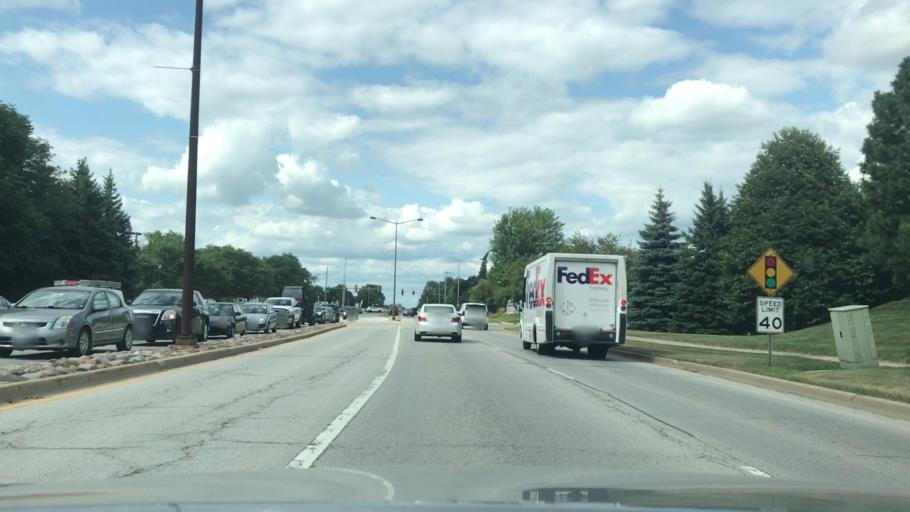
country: US
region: Illinois
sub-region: Kane County
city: Aurora
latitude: 41.7570
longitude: -88.2432
